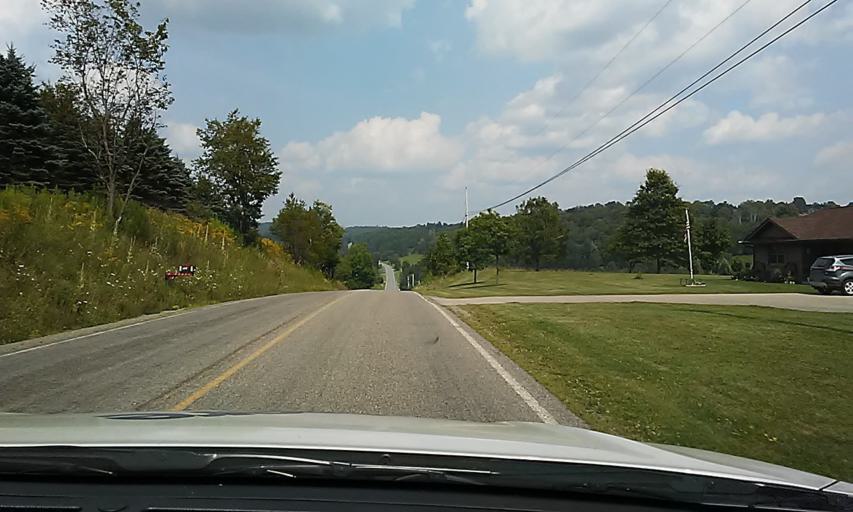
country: US
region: Pennsylvania
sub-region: Potter County
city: Coudersport
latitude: 41.7287
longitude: -78.0193
